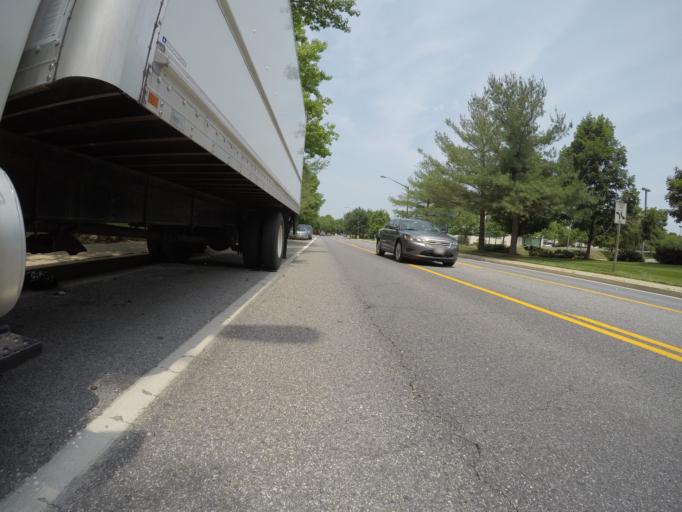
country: US
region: Maryland
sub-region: Howard County
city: Columbia
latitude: 39.2310
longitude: -76.8152
